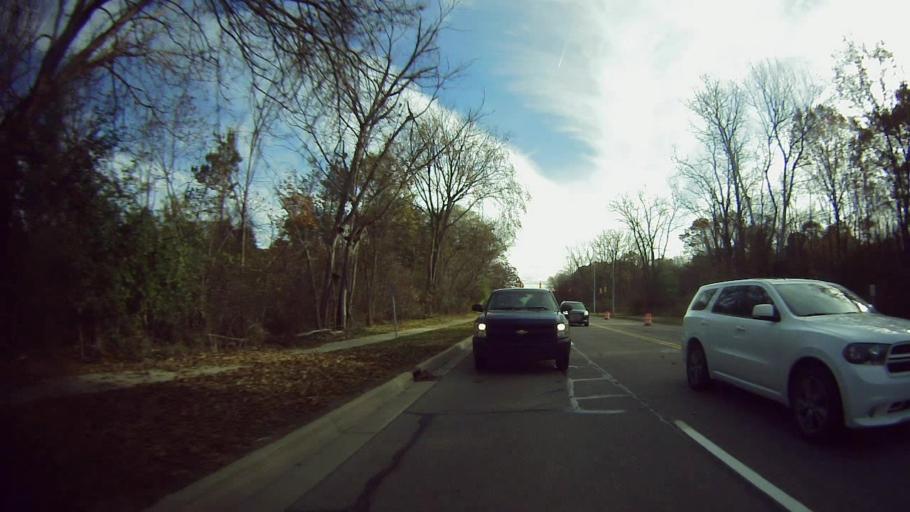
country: US
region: Michigan
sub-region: Oakland County
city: Southfield
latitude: 42.4582
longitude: -83.2437
